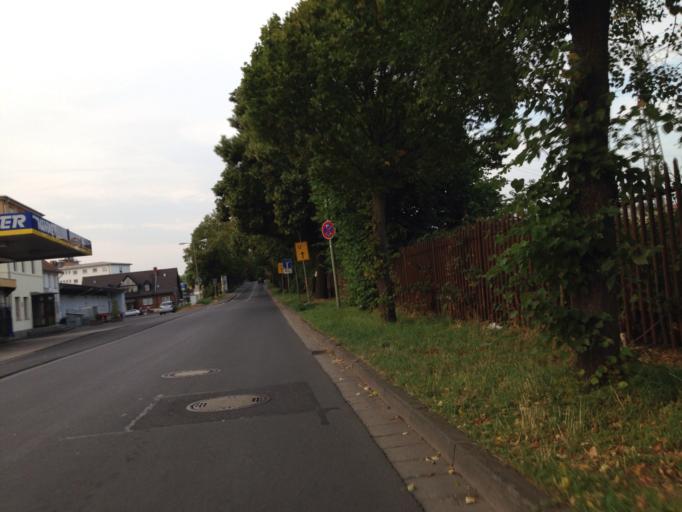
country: DE
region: Hesse
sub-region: Regierungsbezirk Giessen
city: Giessen
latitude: 50.5763
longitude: 8.6571
